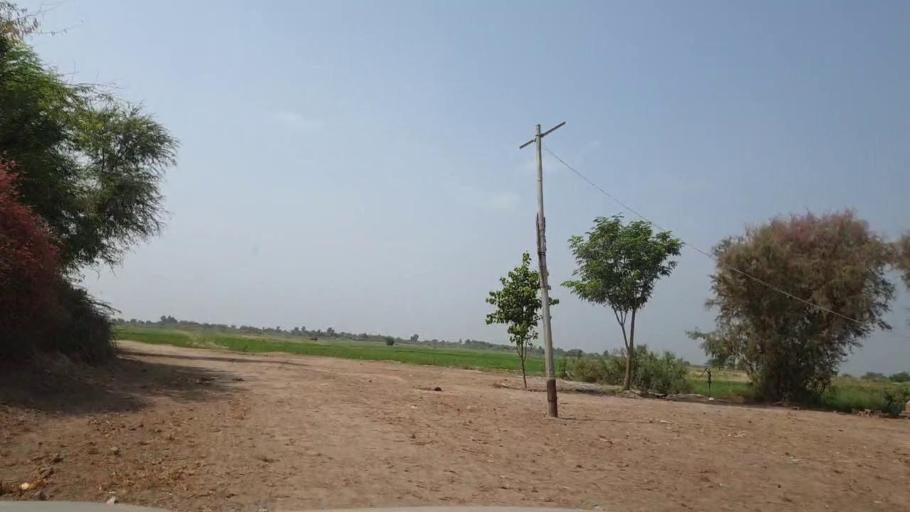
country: PK
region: Sindh
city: Dokri
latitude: 27.4130
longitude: 68.2015
